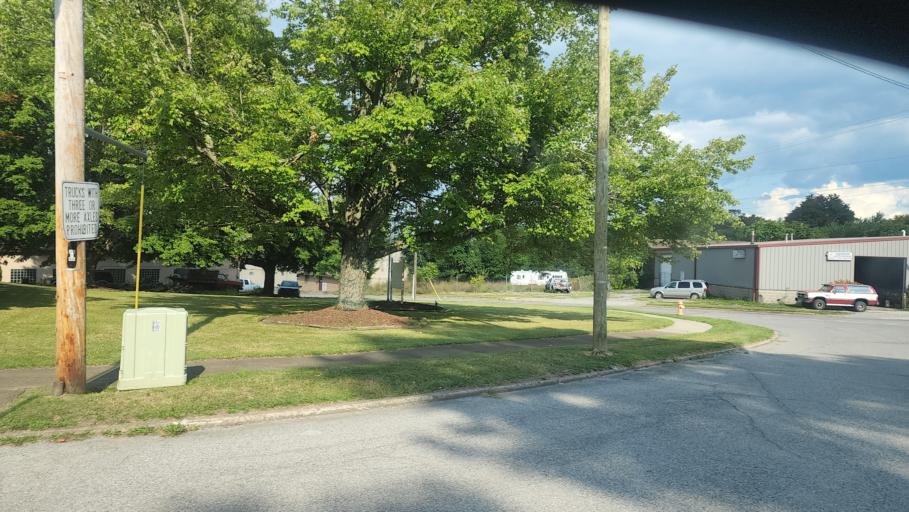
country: US
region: Ohio
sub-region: Mahoning County
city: Struthers
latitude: 41.0616
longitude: -80.6050
